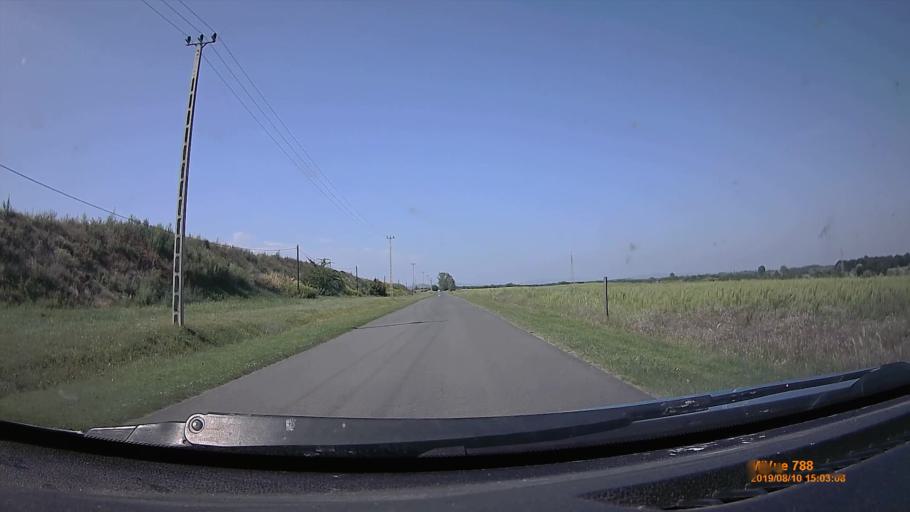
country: HU
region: Somogy
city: Lengyeltoti
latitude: 46.6621
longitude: 17.5730
